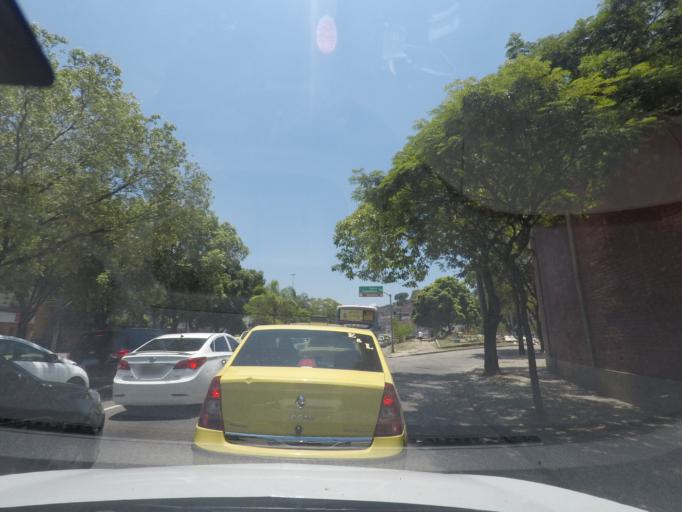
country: BR
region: Rio de Janeiro
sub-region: Rio De Janeiro
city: Rio de Janeiro
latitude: -22.9099
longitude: -43.2382
